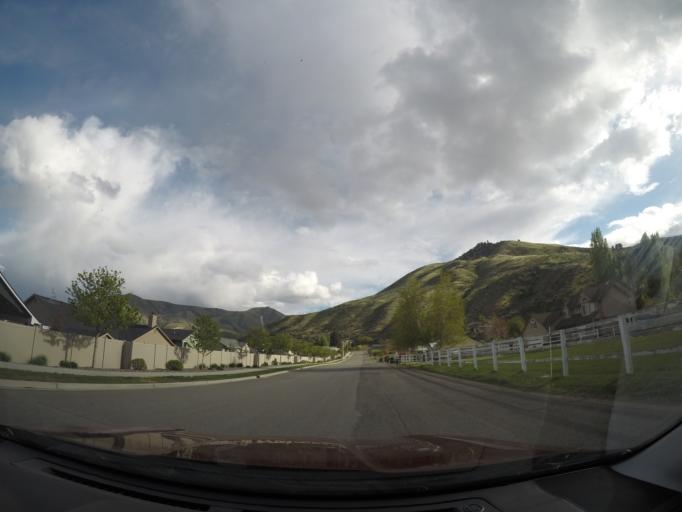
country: US
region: Washington
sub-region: Chelan County
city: South Wenatchee
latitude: 47.3967
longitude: -120.3138
